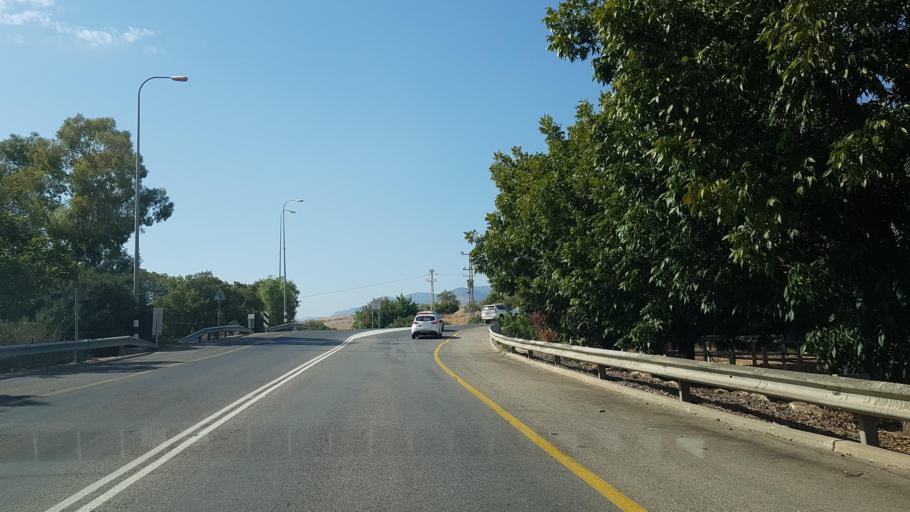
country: IL
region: Northern District
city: Rosh Pinna
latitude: 32.9045
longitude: 35.5488
